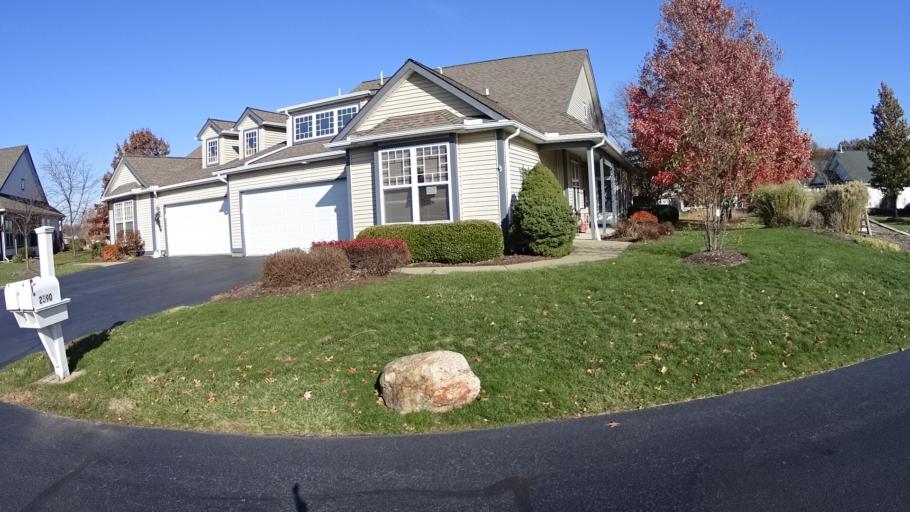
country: US
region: Ohio
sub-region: Lorain County
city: Avon Center
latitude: 41.4564
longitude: -82.0042
